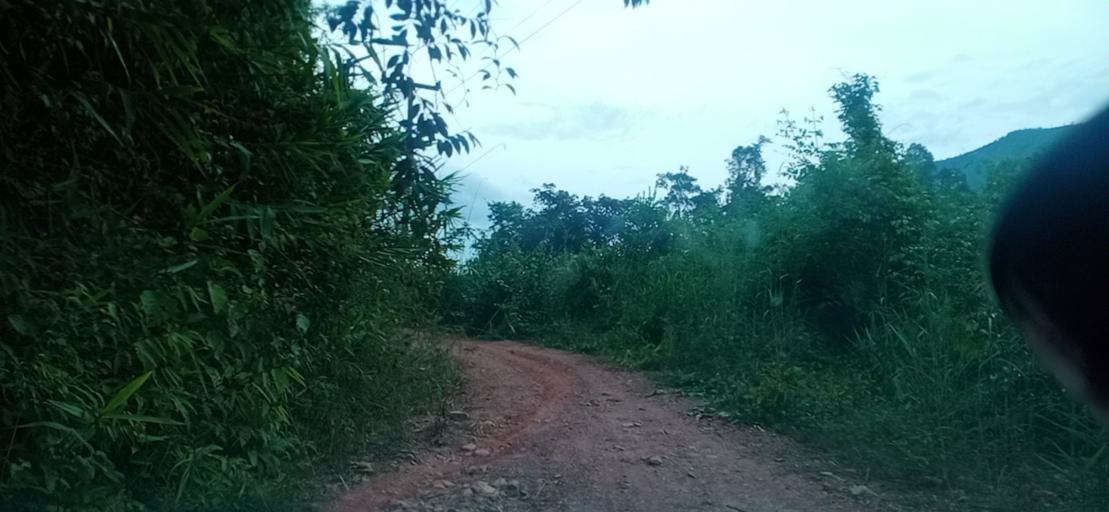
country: TH
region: Changwat Bueng Kan
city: Pak Khat
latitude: 18.5617
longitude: 103.2643
